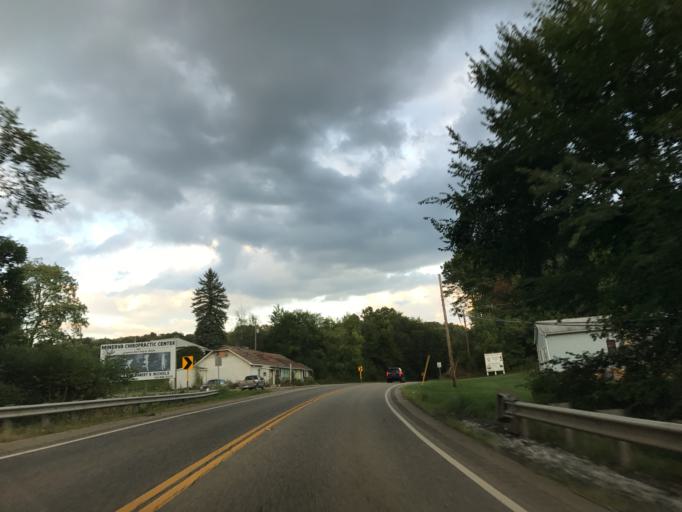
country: US
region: Ohio
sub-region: Stark County
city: Minerva
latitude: 40.7374
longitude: -81.1189
